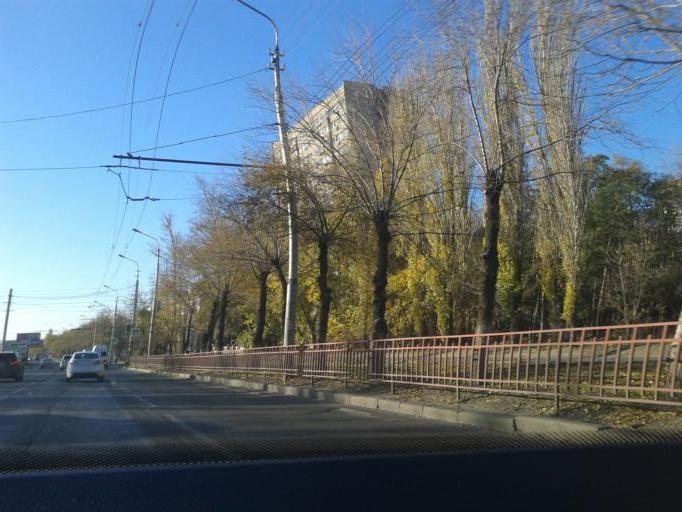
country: RU
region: Volgograd
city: Volgograd
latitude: 48.6161
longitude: 44.4231
